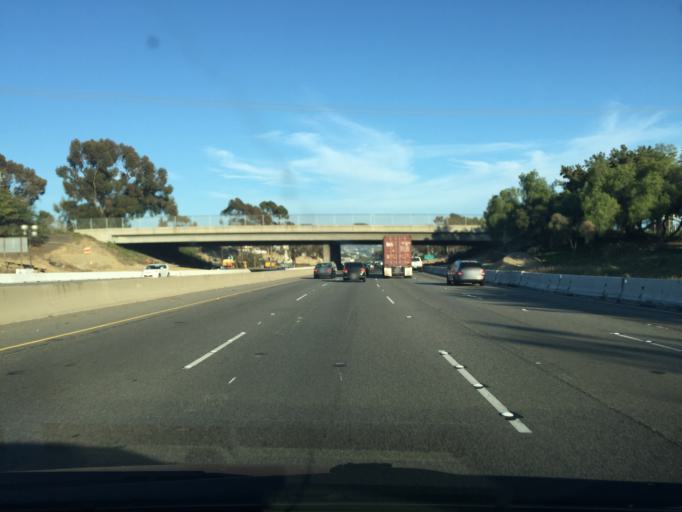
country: US
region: California
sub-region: Orange County
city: Dana Point
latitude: 33.4594
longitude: -117.6573
